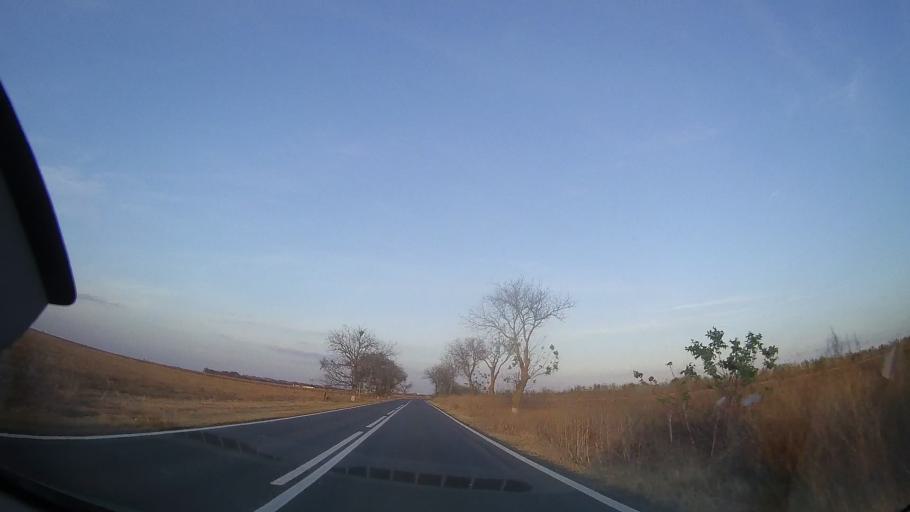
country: RO
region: Constanta
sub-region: Comuna Topraisar
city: Topraisar
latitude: 43.9983
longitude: 28.4321
